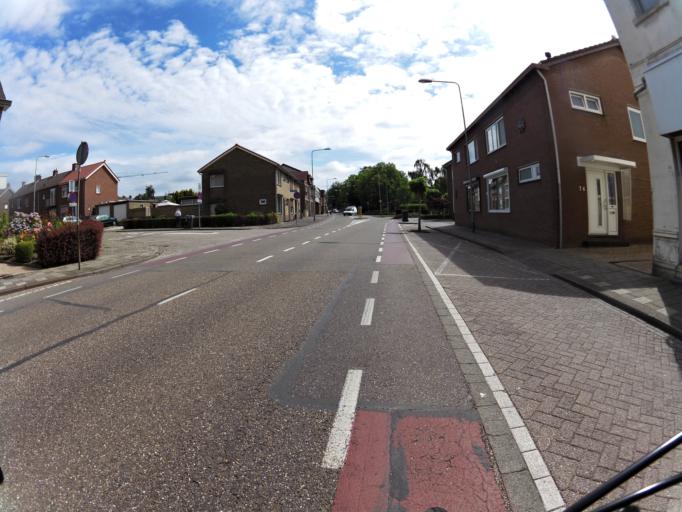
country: NL
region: Limburg
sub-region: Gemeente Heerlen
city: Heerlen
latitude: 50.9002
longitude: 6.0212
